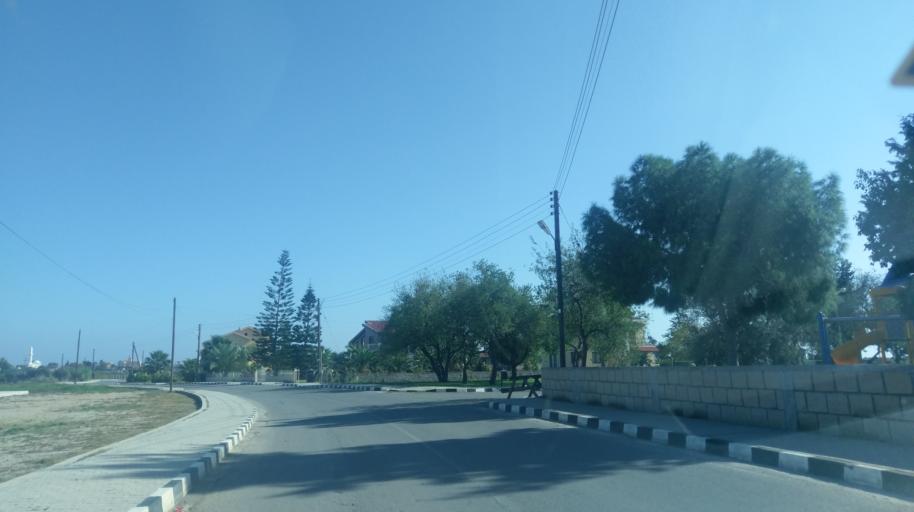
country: CY
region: Ammochostos
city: Trikomo
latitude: 35.2364
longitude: 33.8638
